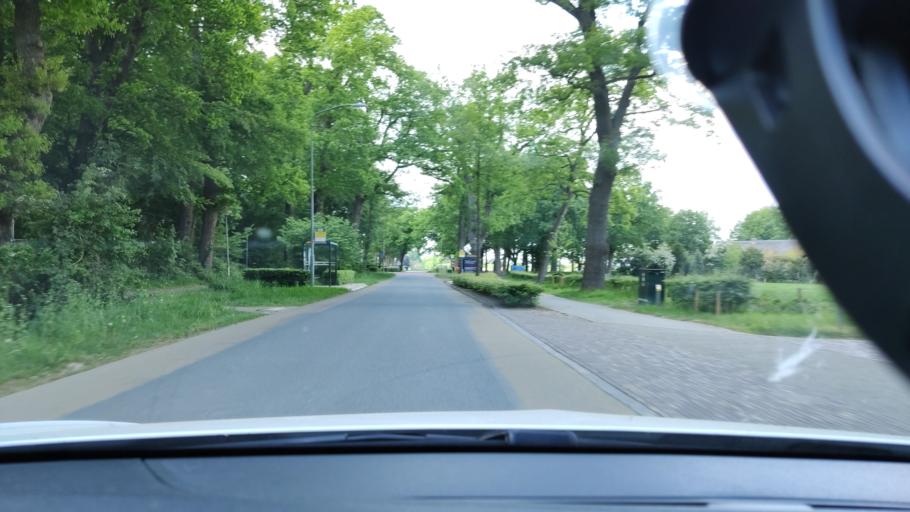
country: NL
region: Drenthe
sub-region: Gemeente Tynaarlo
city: Zuidlaren
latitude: 53.1113
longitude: 6.6760
